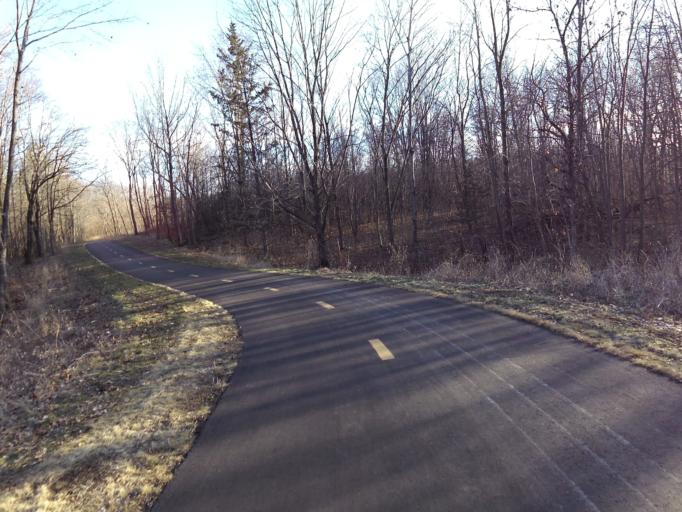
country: US
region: Minnesota
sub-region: Scott County
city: Prior Lake
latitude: 44.7234
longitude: -93.4676
